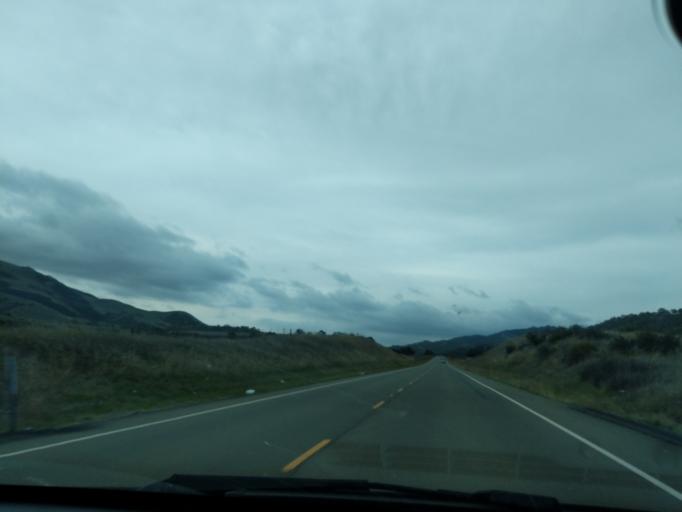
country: US
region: California
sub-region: San Benito County
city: Ridgemark
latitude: 36.6356
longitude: -121.2293
